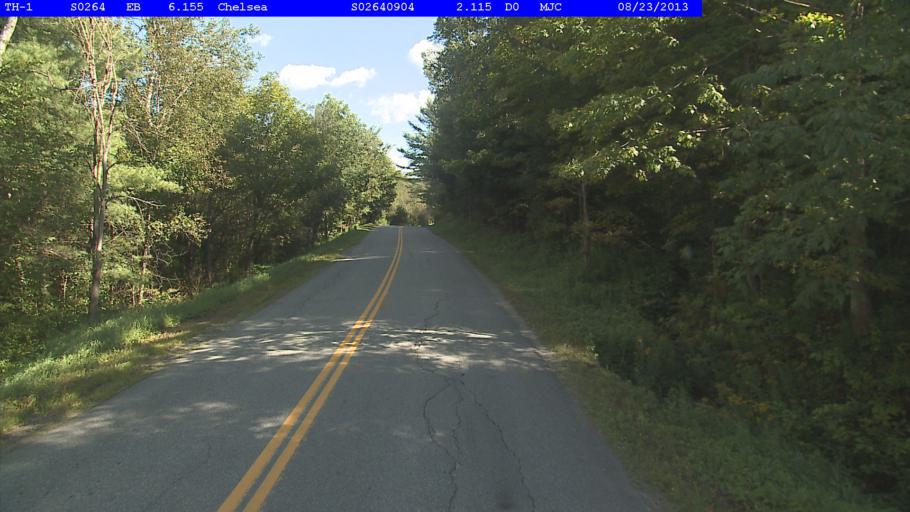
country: US
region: Vermont
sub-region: Orange County
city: Chelsea
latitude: 43.9665
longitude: -72.4771
